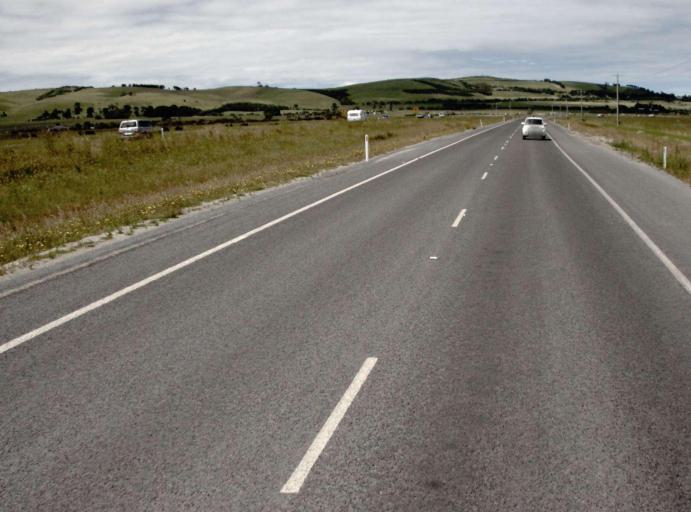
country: AU
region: Victoria
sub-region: Bass Coast
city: North Wonthaggi
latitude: -38.4942
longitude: 145.4629
